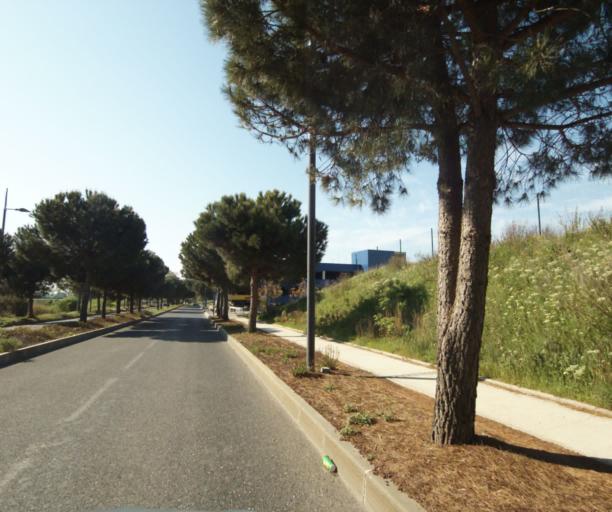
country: FR
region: Languedoc-Roussillon
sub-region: Departement de l'Herault
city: Castelnau-le-Lez
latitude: 43.6058
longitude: 3.9256
